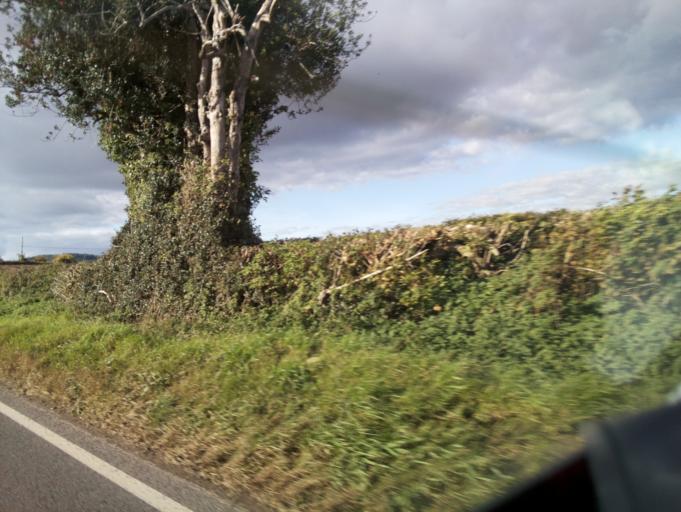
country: GB
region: England
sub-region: Herefordshire
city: Bridge Sollers
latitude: 52.0763
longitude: -2.8441
